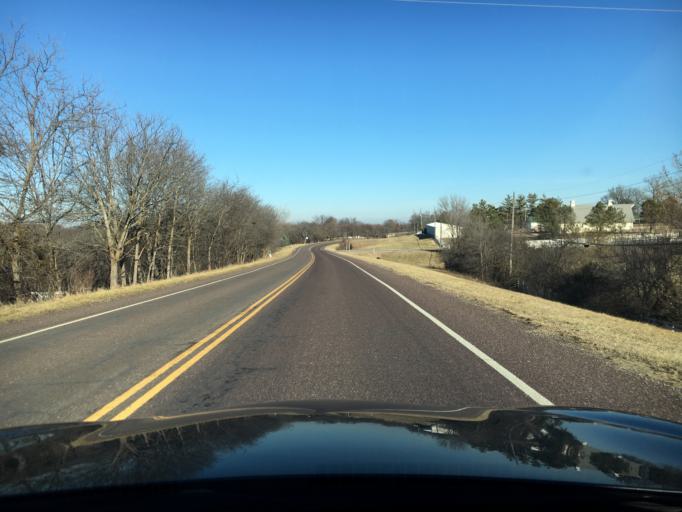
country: US
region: Missouri
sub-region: Cass County
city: Belton
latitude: 38.8049
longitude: -94.6678
